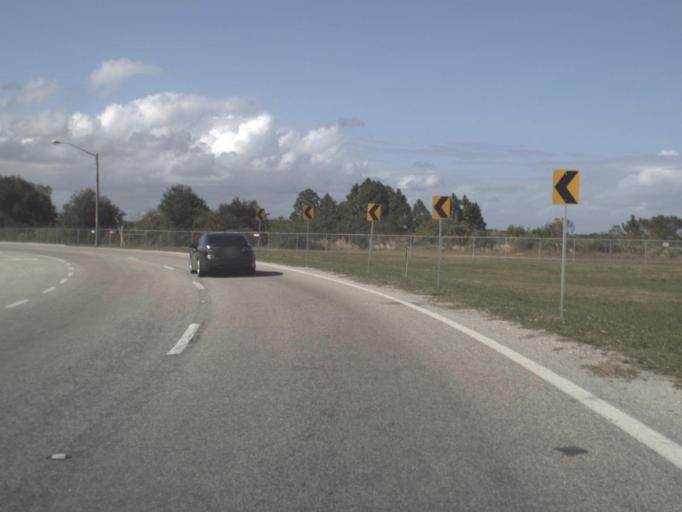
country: US
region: Florida
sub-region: Brevard County
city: West Melbourne
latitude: 28.0978
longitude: -80.6551
